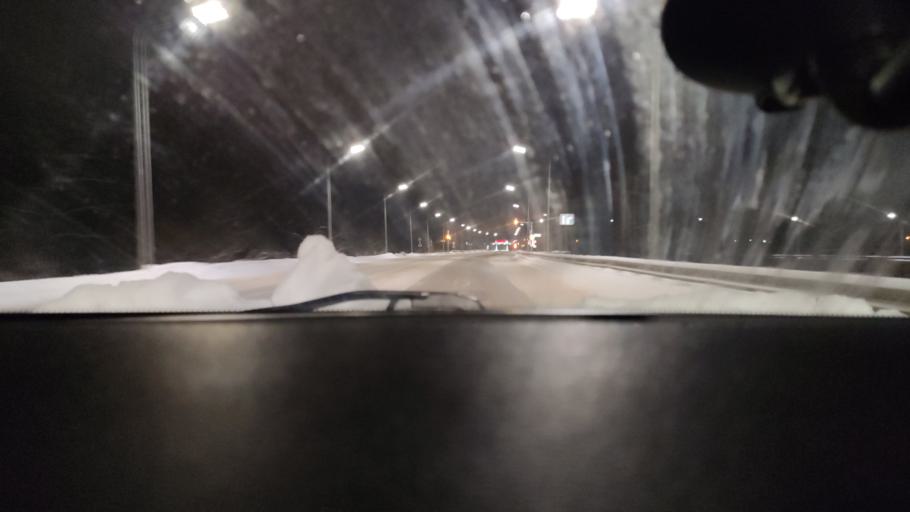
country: RU
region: Perm
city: Overyata
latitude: 58.0589
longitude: 55.8321
